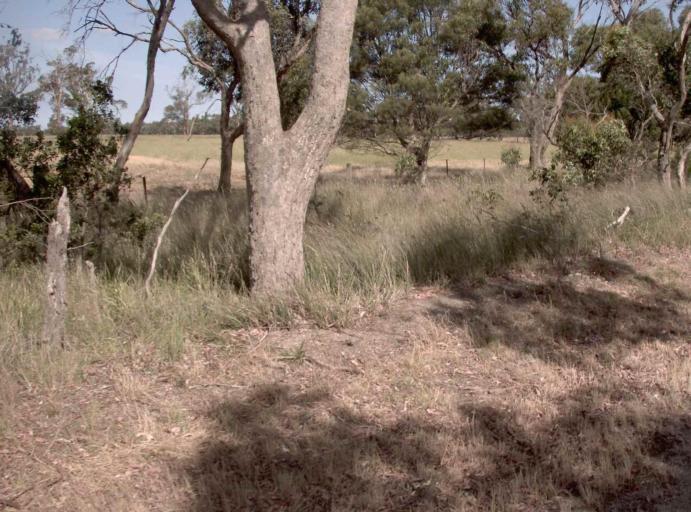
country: AU
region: Victoria
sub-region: Wellington
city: Sale
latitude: -38.2863
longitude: 147.1548
